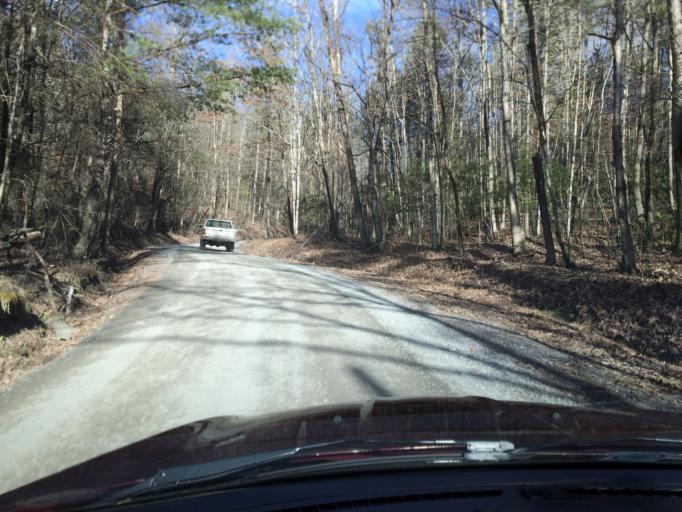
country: US
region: Virginia
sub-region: Alleghany County
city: Clifton Forge
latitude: 37.7189
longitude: -79.8271
